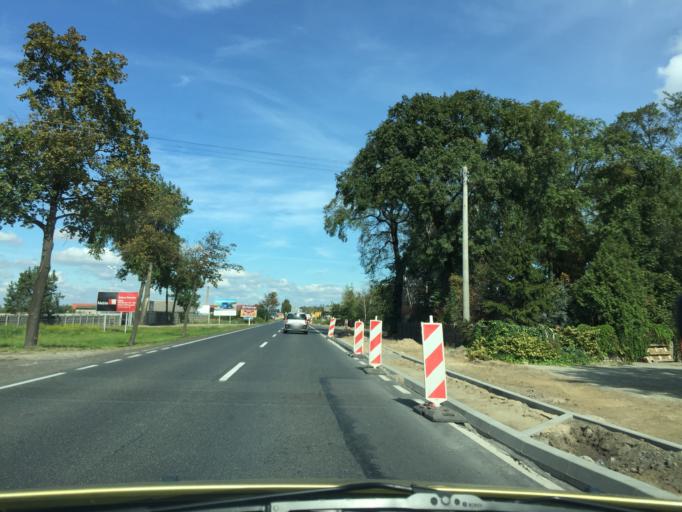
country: PL
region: Greater Poland Voivodeship
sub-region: Kalisz
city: Kalisz
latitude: 51.7953
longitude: 18.0915
